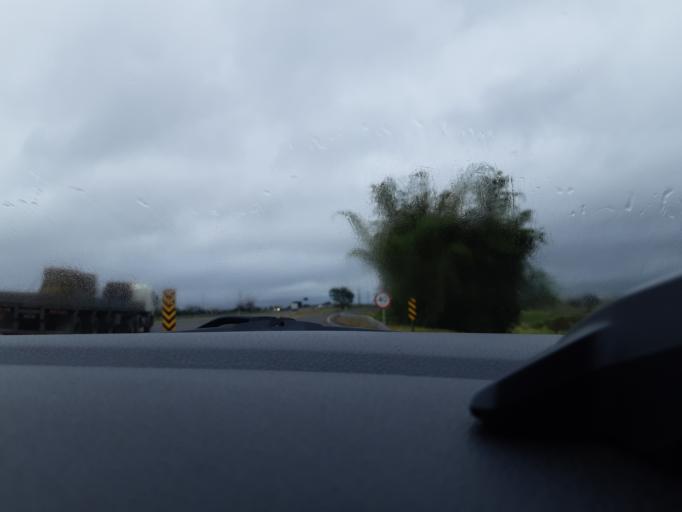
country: BR
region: Sao Paulo
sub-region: Ourinhos
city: Ourinhos
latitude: -22.9780
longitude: -49.9033
